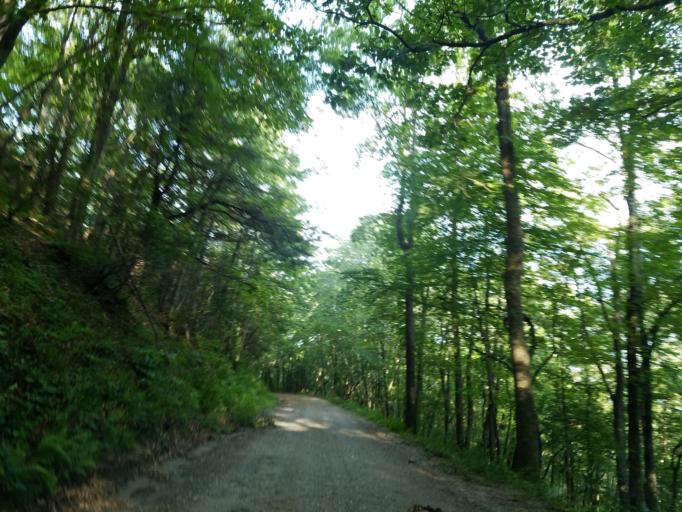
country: US
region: Georgia
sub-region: Lumpkin County
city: Dahlonega
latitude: 34.6593
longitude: -84.1328
